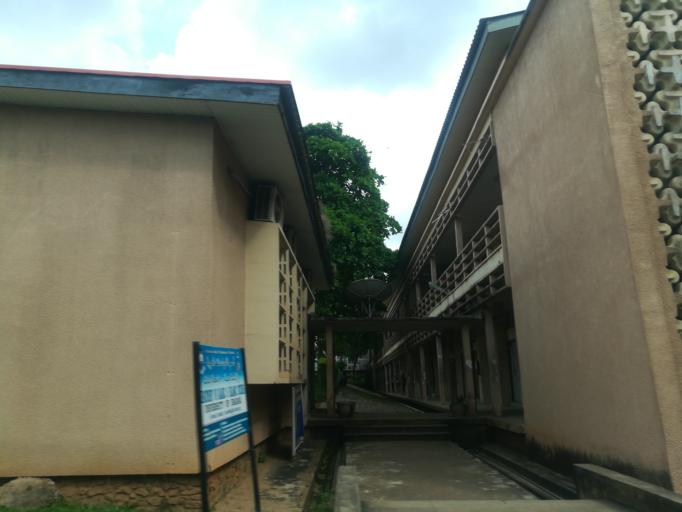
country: NG
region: Oyo
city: Ibadan
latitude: 7.4439
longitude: 3.8984
